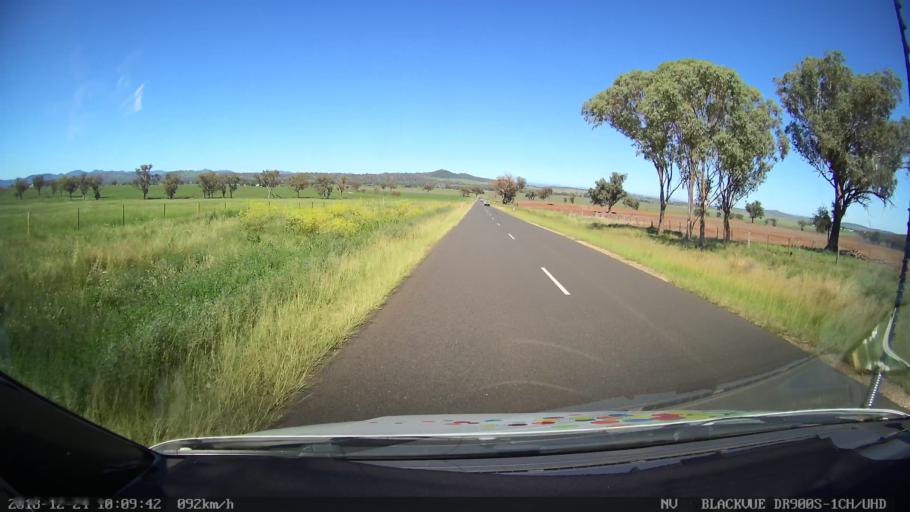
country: AU
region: New South Wales
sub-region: Liverpool Plains
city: Quirindi
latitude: -31.6647
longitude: 150.6868
